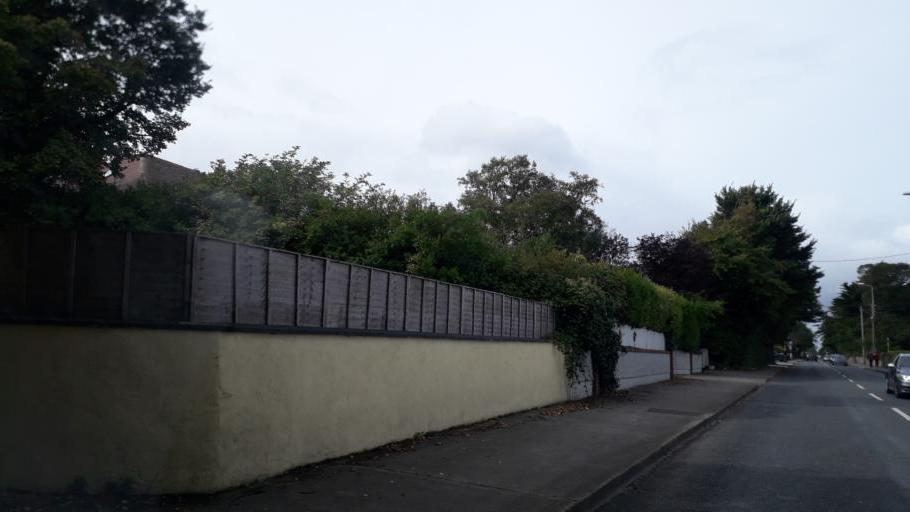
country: IE
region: Leinster
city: Sallynoggin
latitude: 53.2720
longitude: -6.1449
